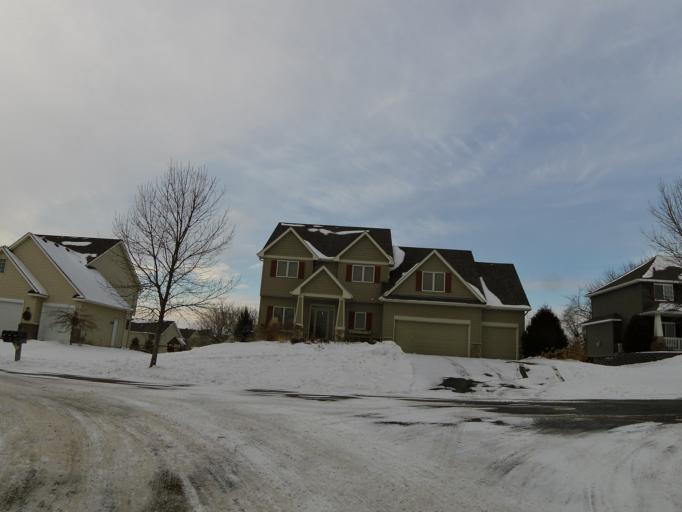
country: US
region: Minnesota
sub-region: Hennepin County
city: Saint Bonifacius
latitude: 44.8982
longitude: -93.7591
